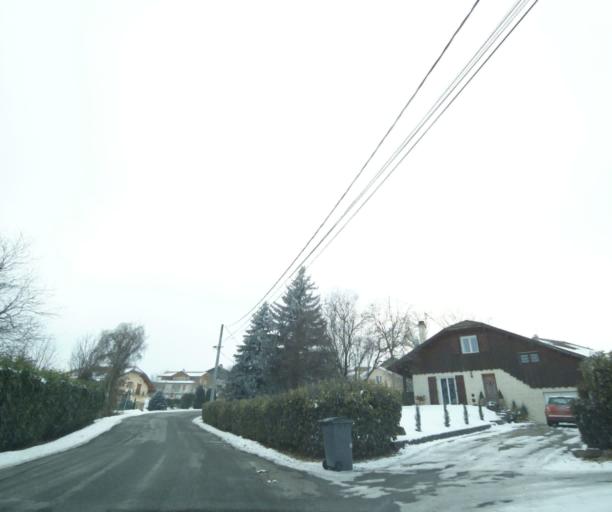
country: FR
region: Rhone-Alpes
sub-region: Departement de la Haute-Savoie
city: Reignier-Esery
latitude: 46.1261
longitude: 6.2468
